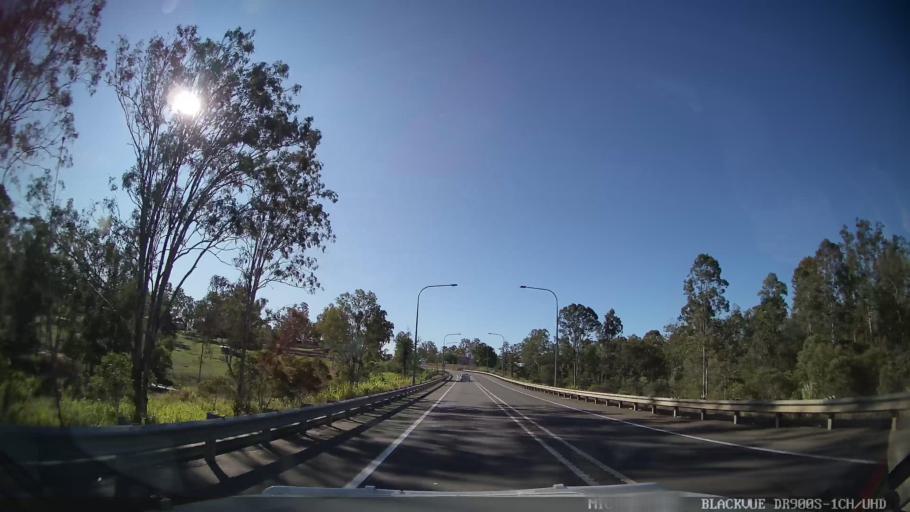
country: AU
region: Queensland
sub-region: Bundaberg
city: Sharon
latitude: -24.9984
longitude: 151.9608
